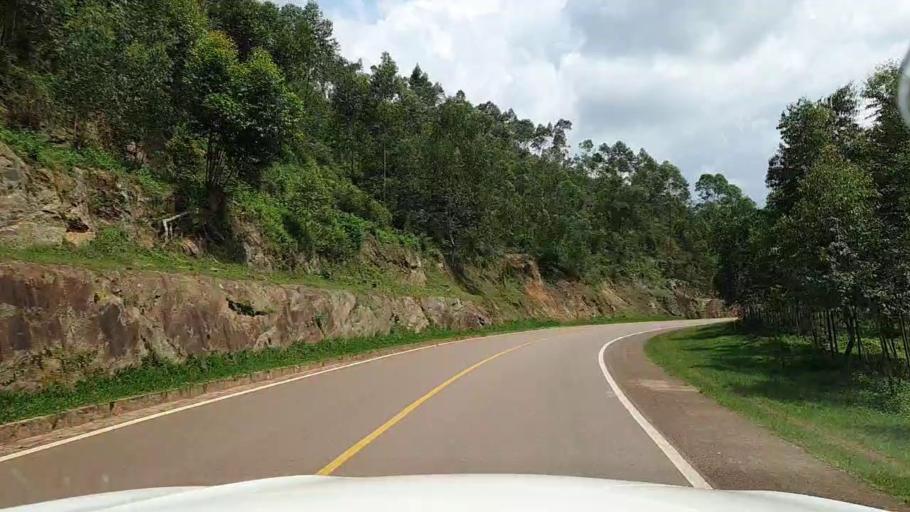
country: RW
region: Kigali
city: Kigali
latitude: -1.8184
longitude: 30.0891
